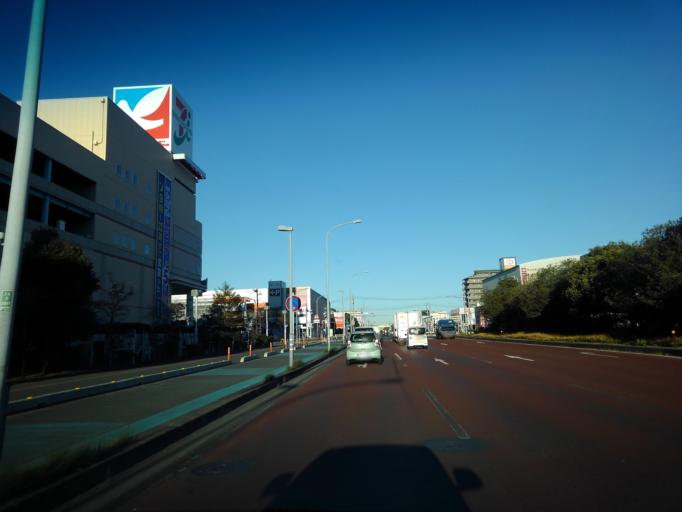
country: JP
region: Chiba
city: Funabashi
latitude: 35.6569
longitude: 140.0521
